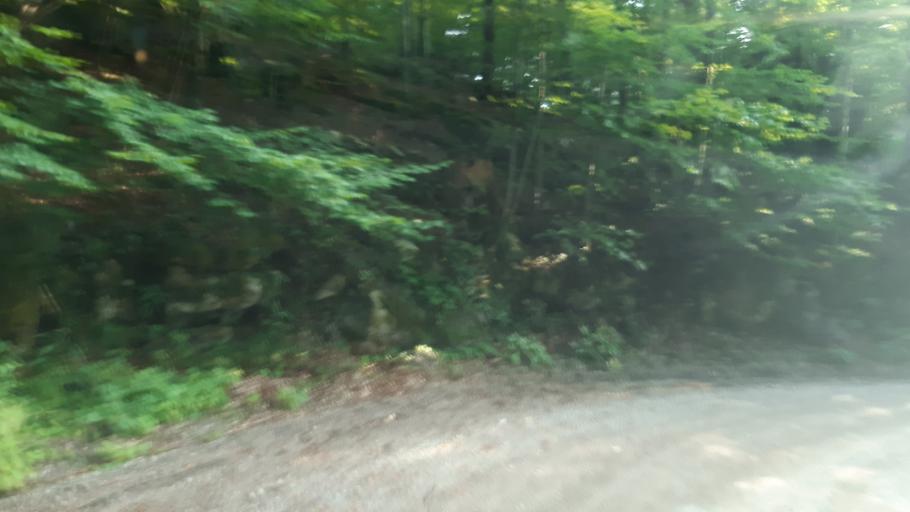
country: SI
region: Dolenjske Toplice
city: Dolenjske Toplice
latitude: 45.6730
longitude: 14.9932
